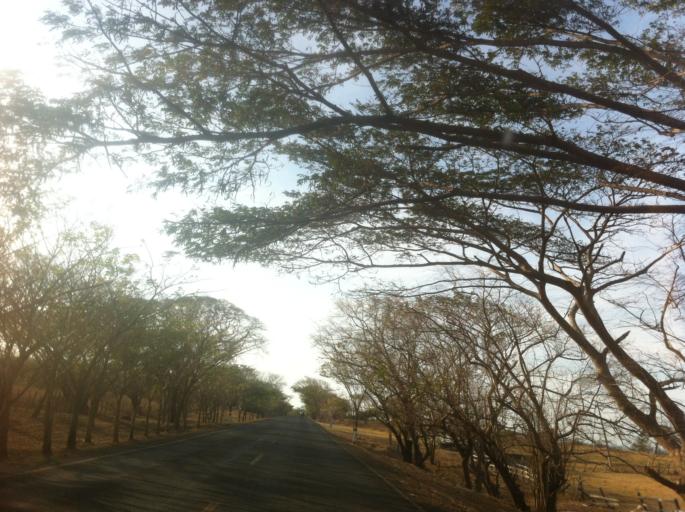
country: NI
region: Rivas
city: Cardenas
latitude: 11.2685
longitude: -85.6485
